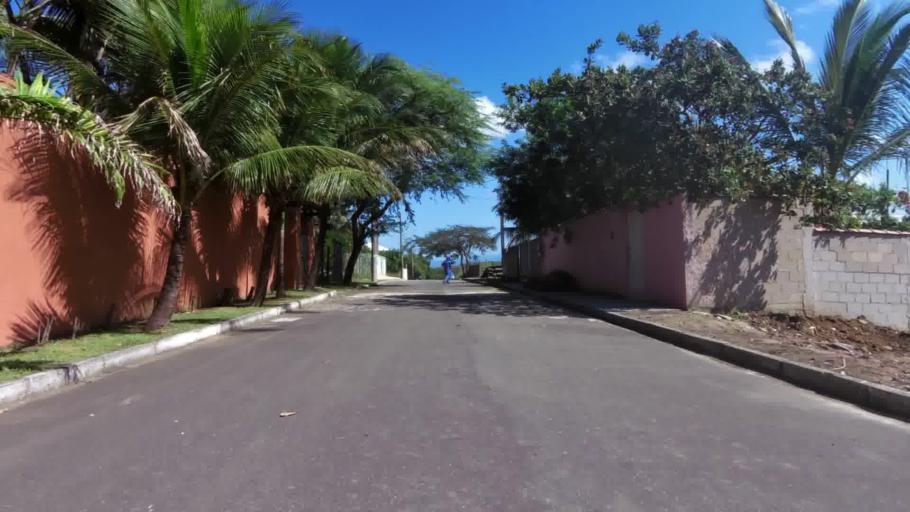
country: BR
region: Espirito Santo
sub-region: Piuma
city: Piuma
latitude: -20.8038
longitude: -40.5996
